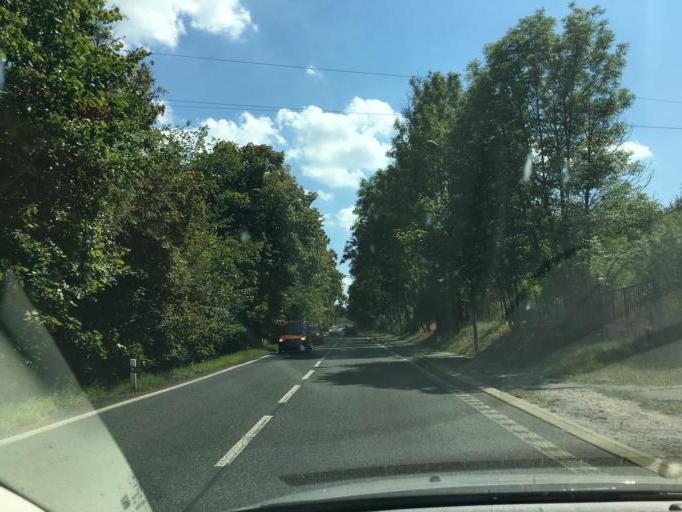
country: CZ
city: Kamenicky Senov
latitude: 50.7780
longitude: 14.4643
